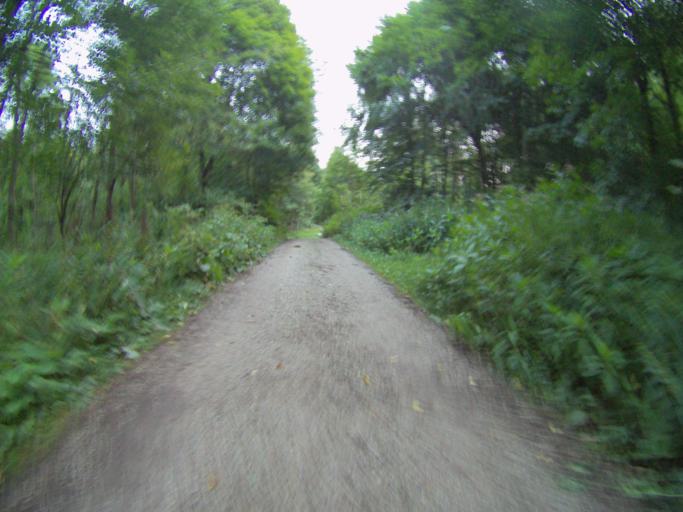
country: DE
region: Bavaria
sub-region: Upper Bavaria
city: Freising
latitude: 48.4201
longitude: 11.7338
